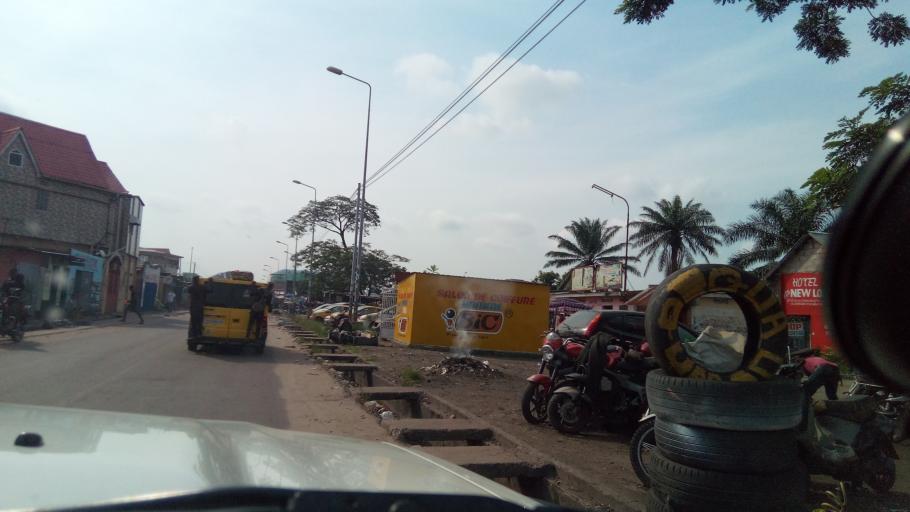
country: CD
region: Kinshasa
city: Kinshasa
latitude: -4.3497
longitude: 15.3210
